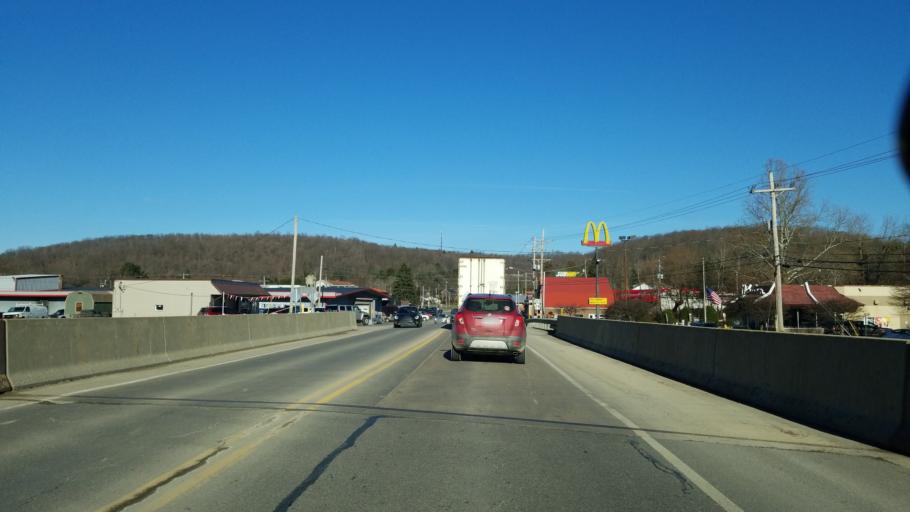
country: US
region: Pennsylvania
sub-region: Jefferson County
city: Brockway
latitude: 41.2448
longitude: -78.7878
